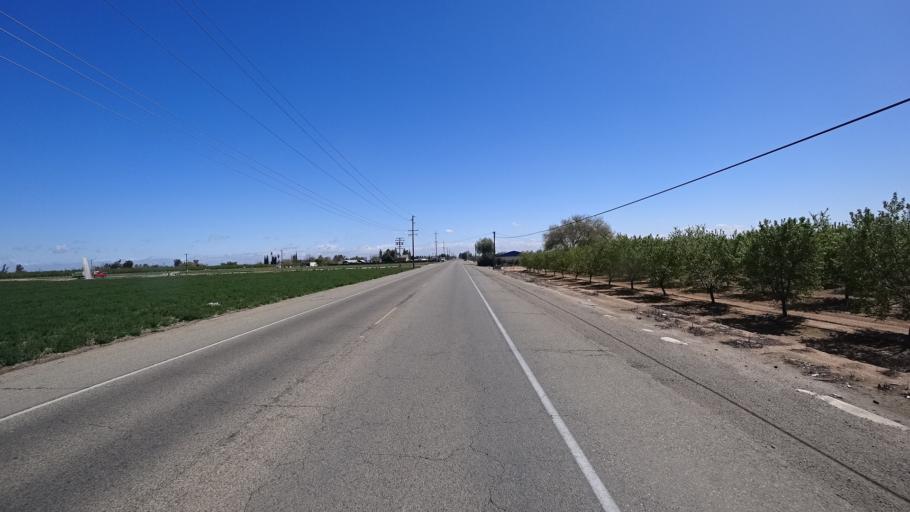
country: US
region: California
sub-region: Fresno County
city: West Park
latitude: 36.7064
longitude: -119.8773
